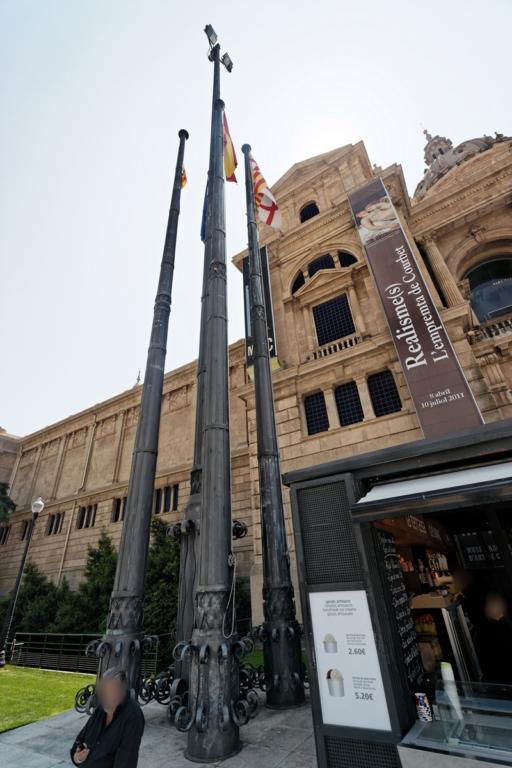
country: ES
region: Catalonia
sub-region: Provincia de Barcelona
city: Sants-Montjuic
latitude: 41.3690
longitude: 2.1533
